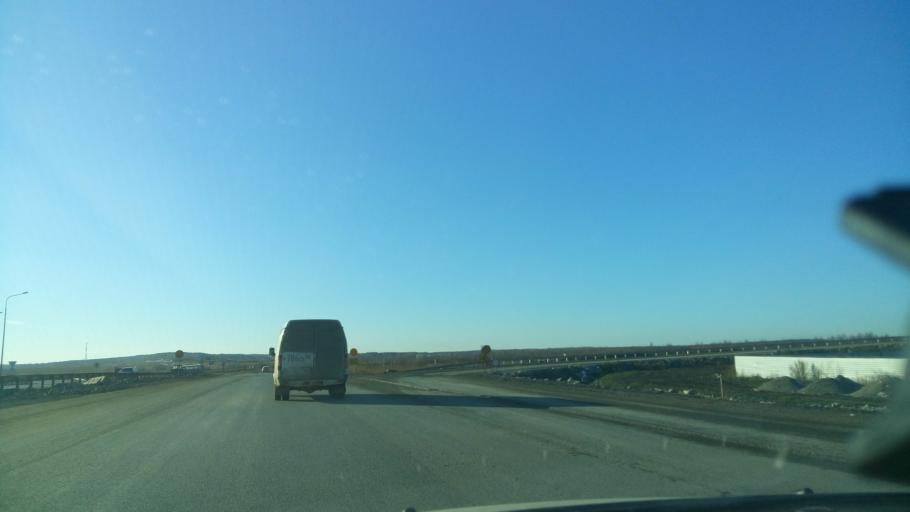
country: RU
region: Sverdlovsk
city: Sovkhoznyy
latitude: 56.7346
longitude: 60.5435
